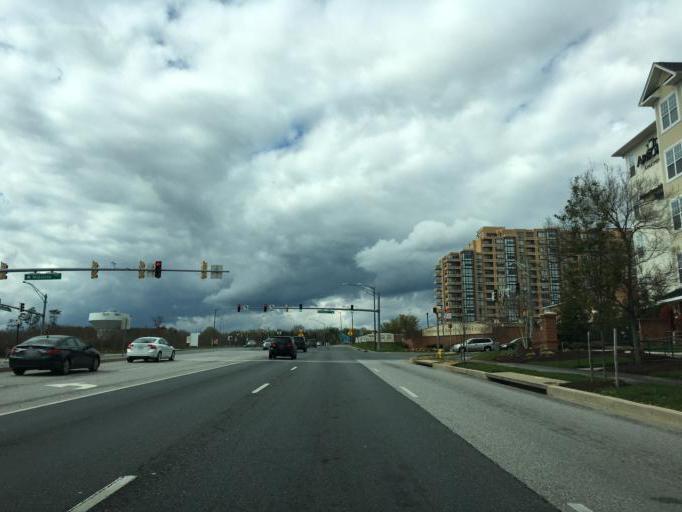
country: US
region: Maryland
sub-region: Anne Arundel County
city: Jessup
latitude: 39.1535
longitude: -76.7424
